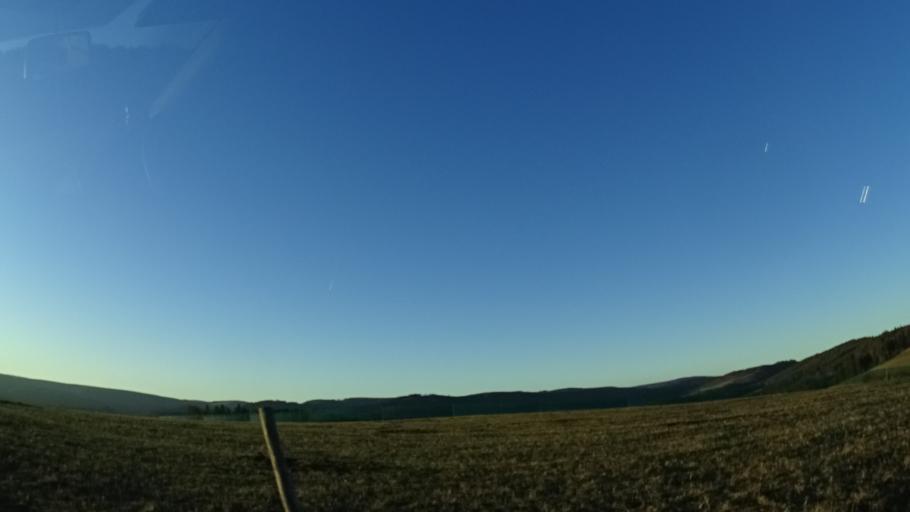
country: DE
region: Thuringia
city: Grafenthal
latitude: 50.5411
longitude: 11.2882
